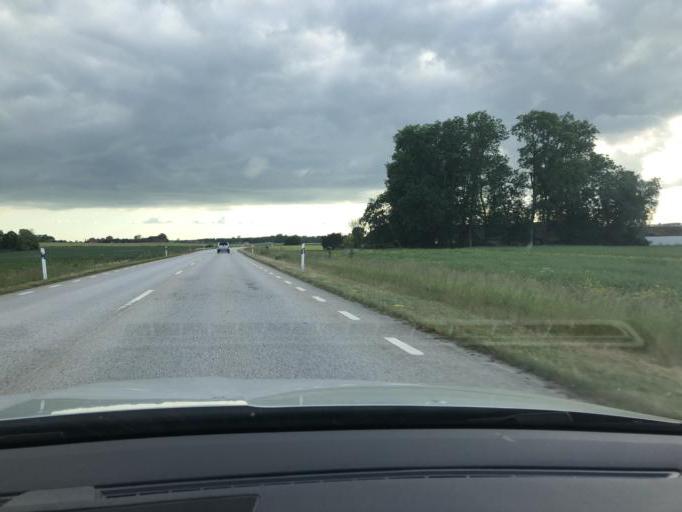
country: SE
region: Skane
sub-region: Simrishamns Kommun
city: Simrishamn
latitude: 55.5370
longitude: 14.3144
